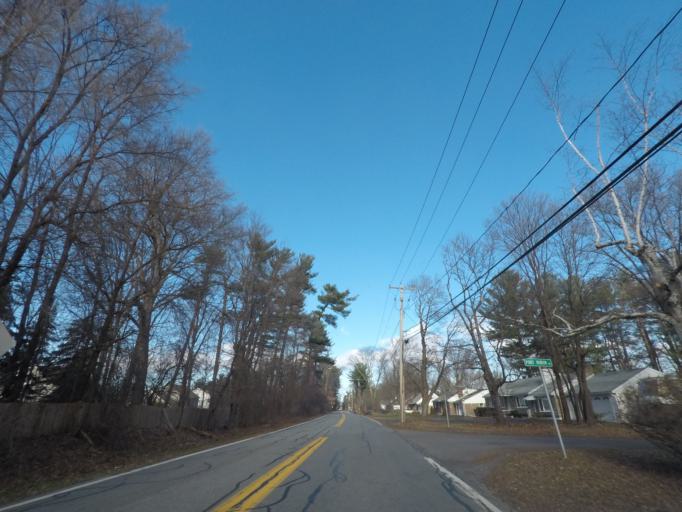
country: US
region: New York
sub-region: Schenectady County
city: Niskayuna
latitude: 42.8202
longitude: -73.8804
